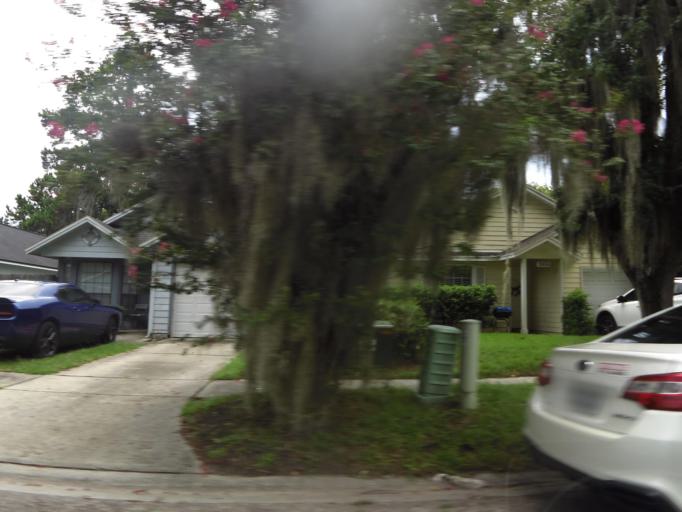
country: US
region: Florida
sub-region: Duval County
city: Jacksonville
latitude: 30.4293
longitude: -81.7000
